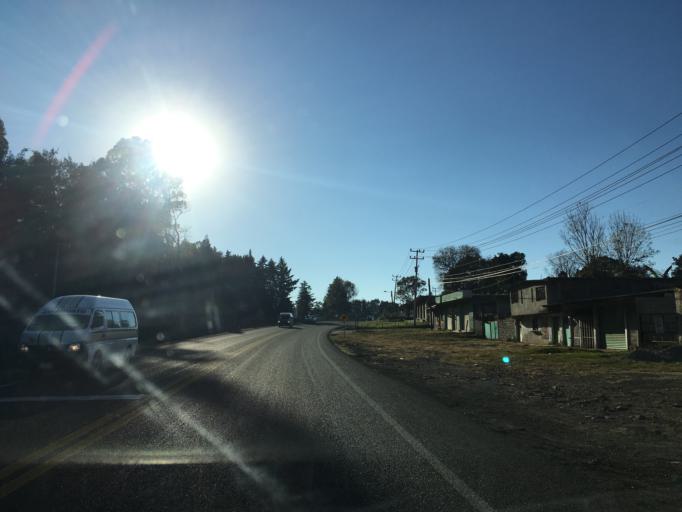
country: MX
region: Michoacan
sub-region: Zitacuaro
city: San Felipe los Alzati (Colonia Nueva)
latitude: 19.4850
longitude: -100.3894
